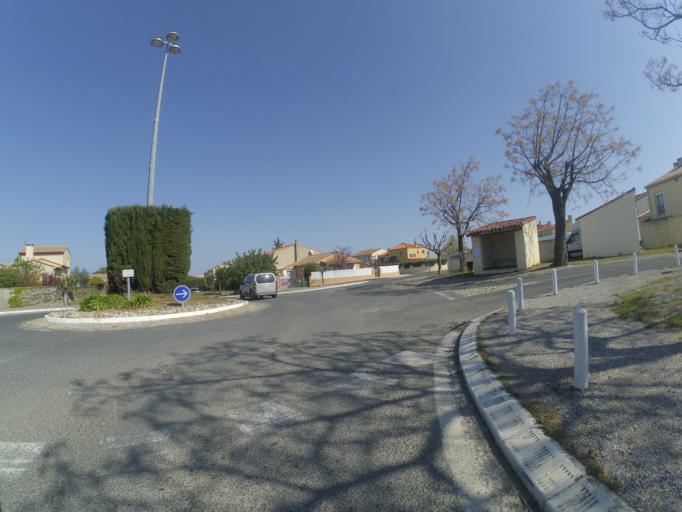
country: FR
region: Languedoc-Roussillon
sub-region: Departement des Pyrenees-Orientales
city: Llupia
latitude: 42.6167
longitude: 2.7691
